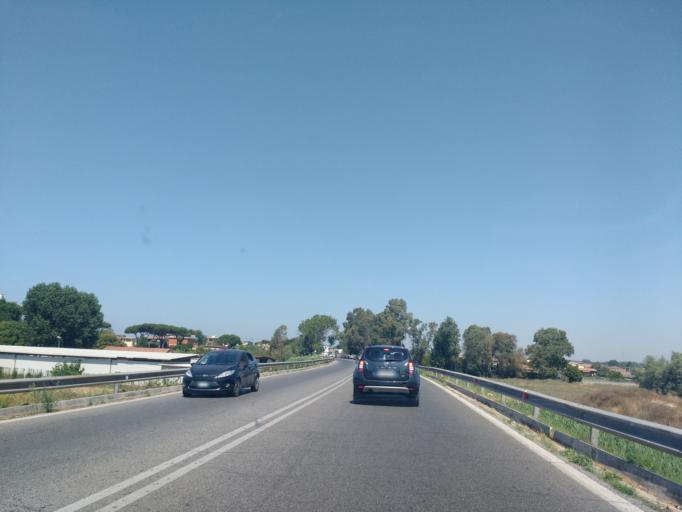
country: IT
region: Latium
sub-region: Citta metropolitana di Roma Capitale
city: Lido di Ostia
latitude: 41.7564
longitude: 12.2759
